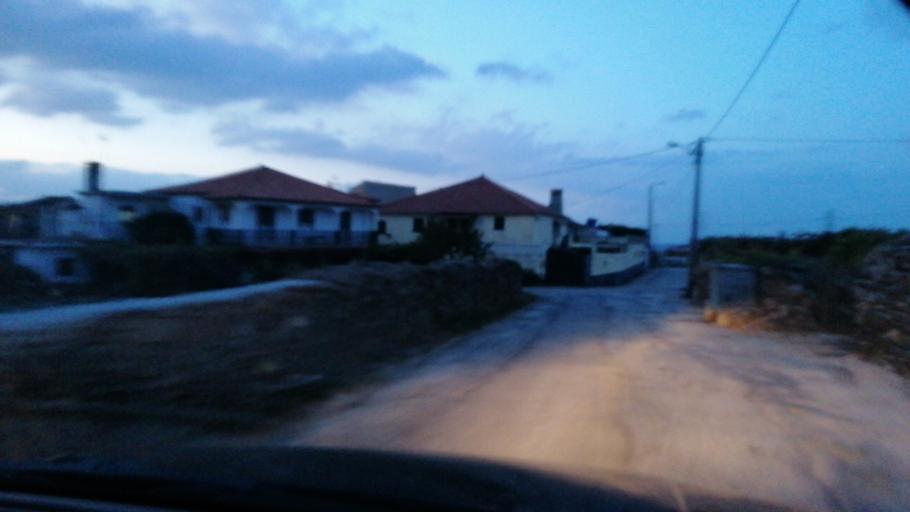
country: PT
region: Viseu
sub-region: Armamar
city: Armamar
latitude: 41.1165
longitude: -7.7151
